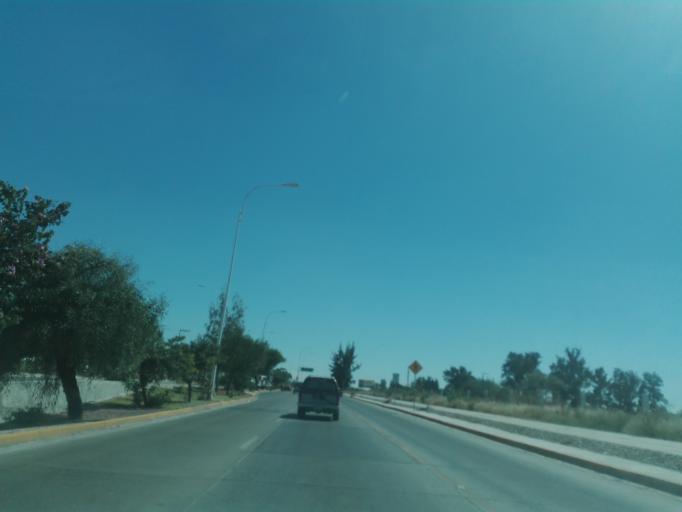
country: MX
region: Guanajuato
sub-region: Leon
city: San Jose de Duran (Los Troncoso)
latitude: 21.0771
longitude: -101.6535
